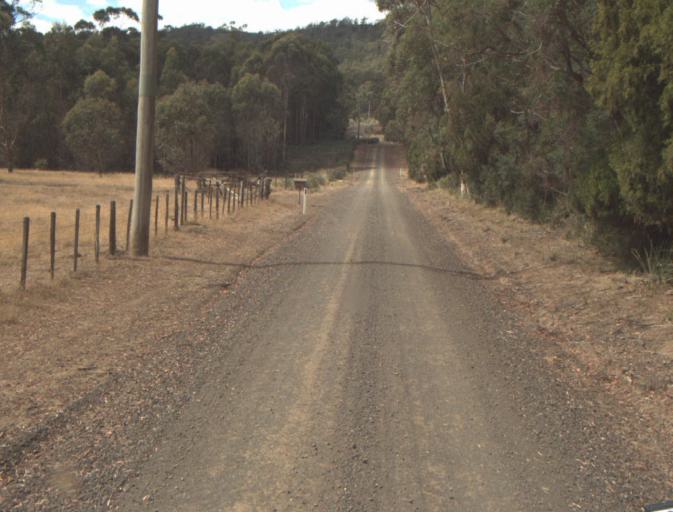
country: AU
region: Tasmania
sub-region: Launceston
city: Mayfield
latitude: -41.2776
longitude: 147.0464
